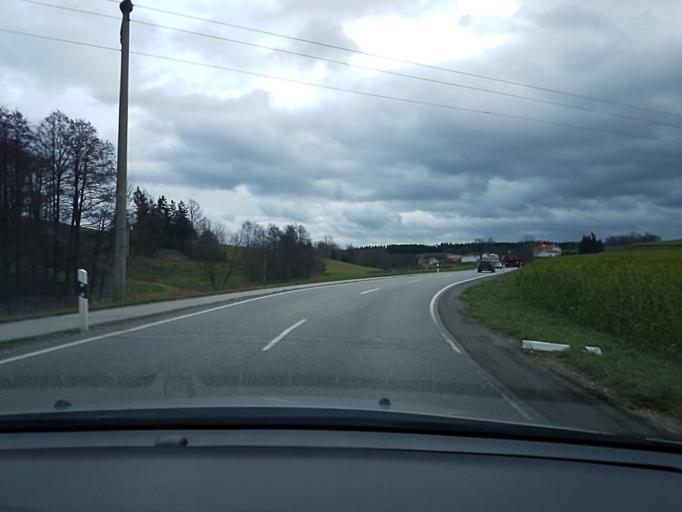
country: DE
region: Bavaria
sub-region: Lower Bavaria
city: Vilsbiburg
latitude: 48.4249
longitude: 12.3544
